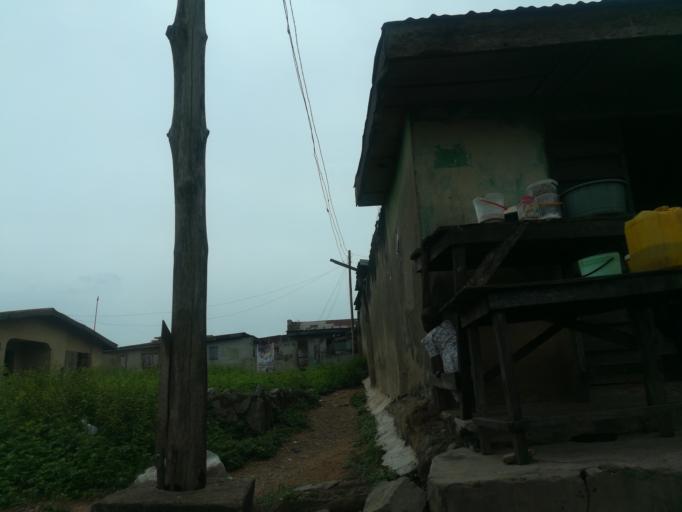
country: NG
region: Oyo
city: Ibadan
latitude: 7.3750
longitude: 3.9312
